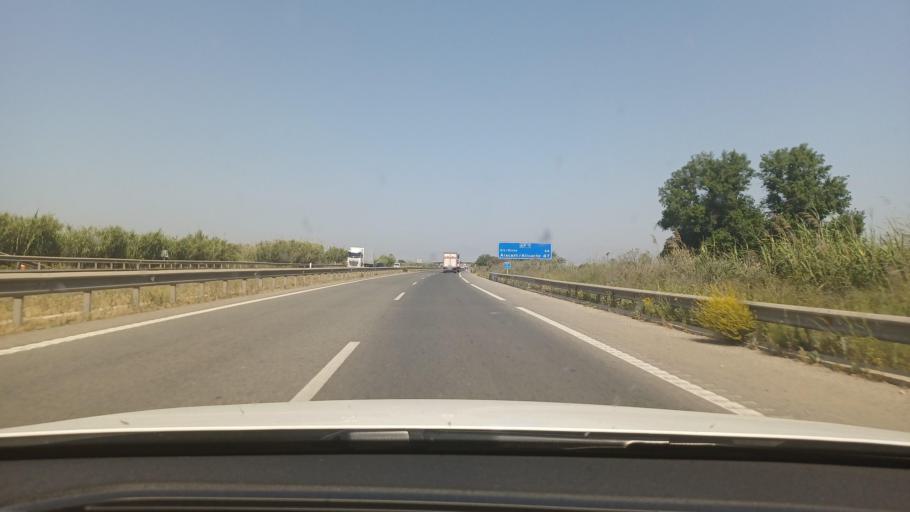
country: ES
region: Valencia
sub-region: Provincia de Alicante
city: Dolores
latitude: 38.1287
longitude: -0.7874
